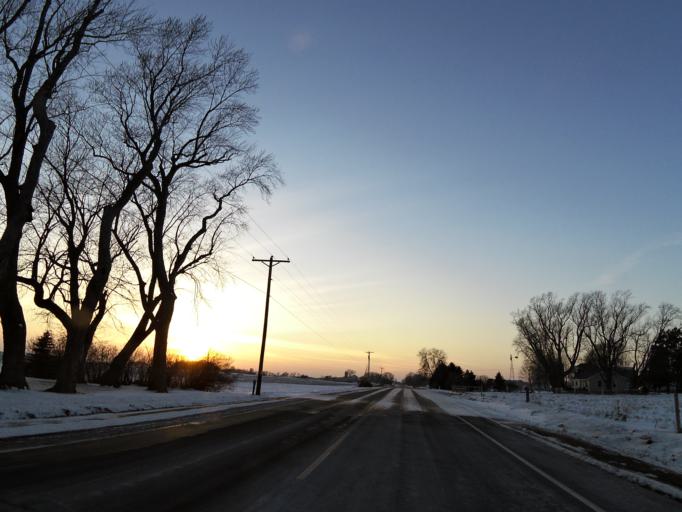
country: US
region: Wisconsin
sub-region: Pierce County
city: River Falls
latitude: 44.8771
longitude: -92.6941
